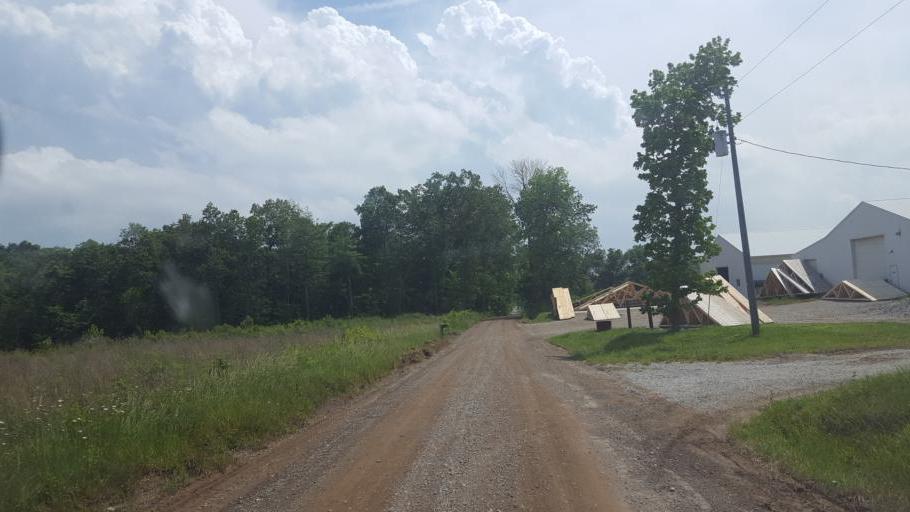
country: US
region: Ohio
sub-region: Knox County
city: Oak Hill
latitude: 40.3215
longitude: -82.2397
